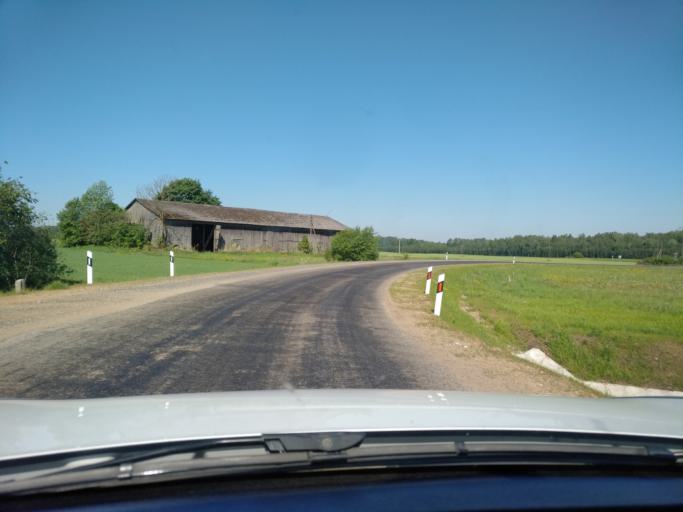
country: LT
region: Panevezys
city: Rokiskis
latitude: 55.7327
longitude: 25.5178
